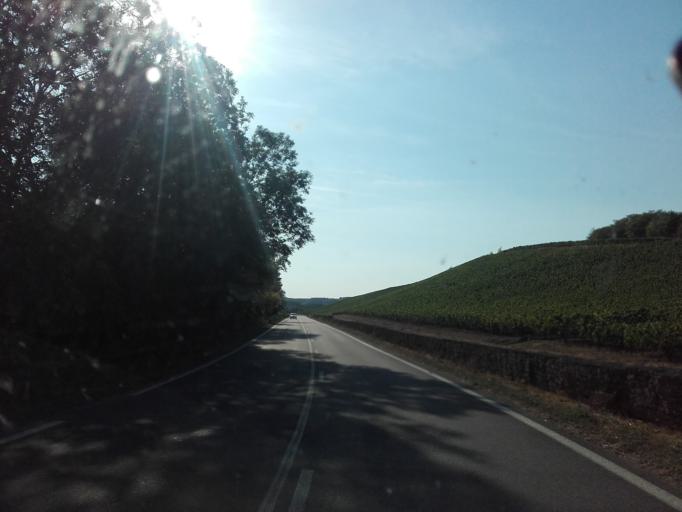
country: FR
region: Bourgogne
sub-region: Departement de l'Yonne
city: Chablis
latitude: 47.8230
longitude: 3.7985
